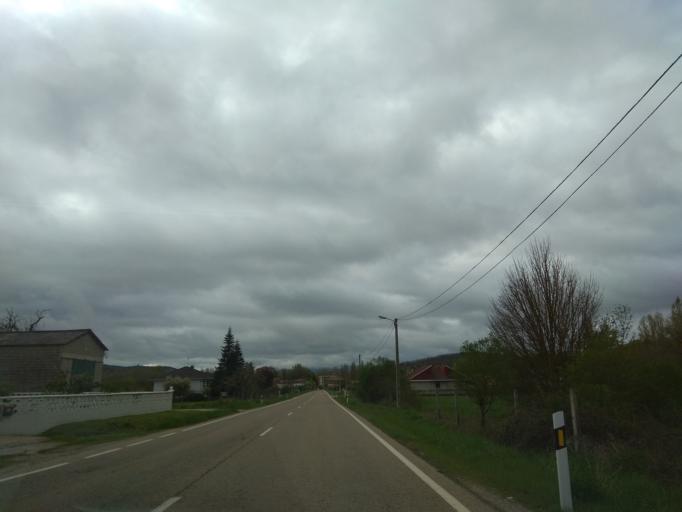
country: ES
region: Castille and Leon
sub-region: Provincia de Burgos
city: Espinosa de los Monteros
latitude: 43.0299
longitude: -3.4836
